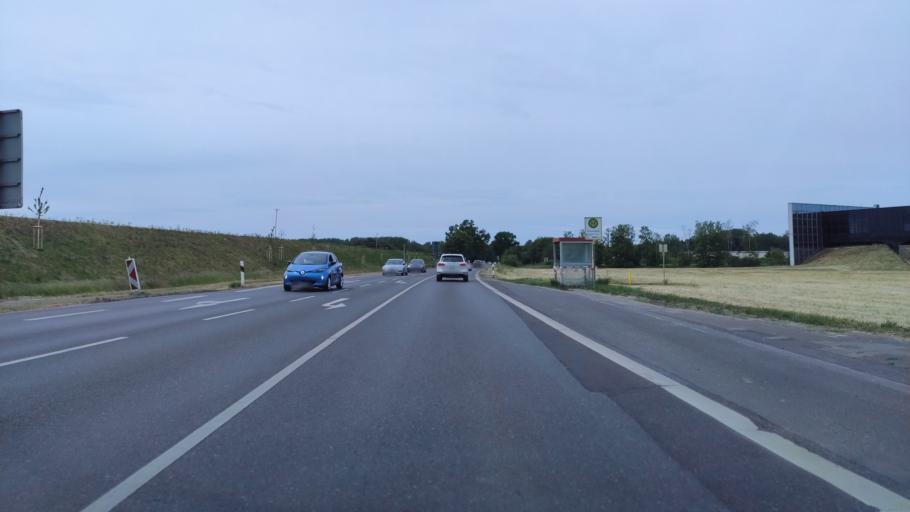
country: DE
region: North Rhine-Westphalia
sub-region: Regierungsbezirk Dusseldorf
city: Korschenbroich
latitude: 51.1929
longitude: 6.5049
